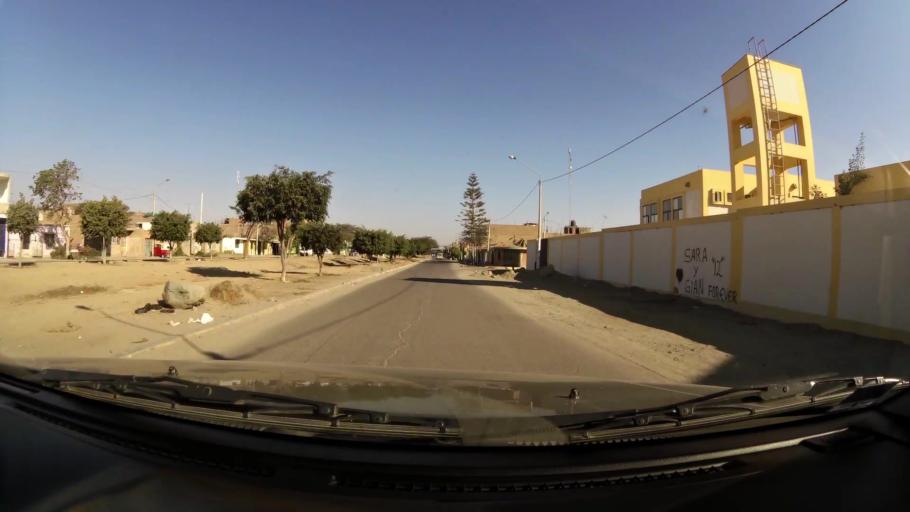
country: PE
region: Ica
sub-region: Provincia de Ica
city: La Tinguina
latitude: -14.0403
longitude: -75.7068
